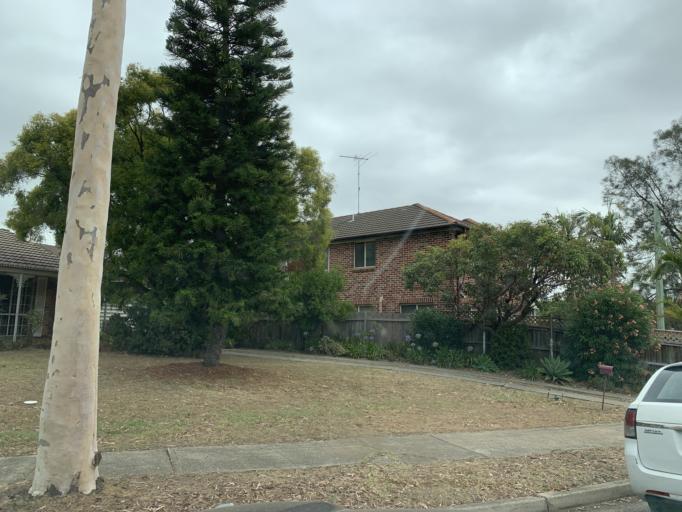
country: AU
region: New South Wales
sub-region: Blacktown
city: Blacktown
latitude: -33.7687
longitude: 150.8993
